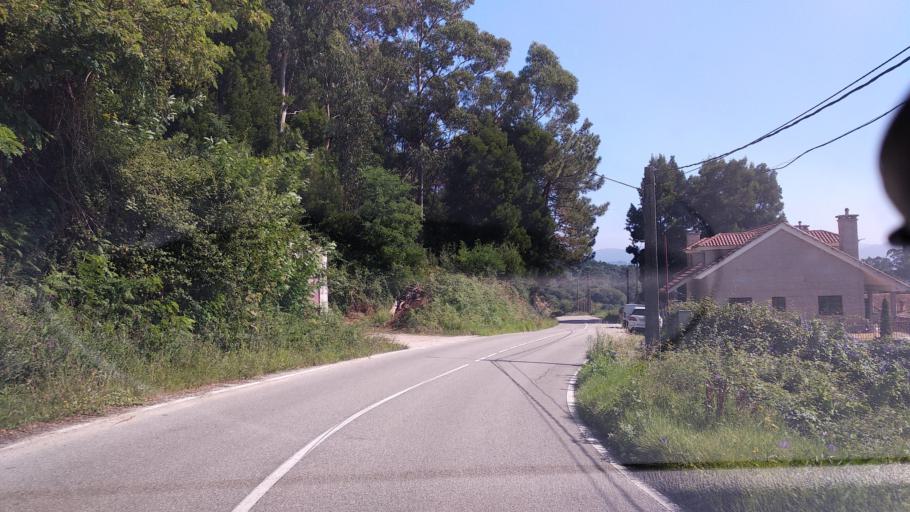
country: ES
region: Galicia
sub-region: Provincia de Pontevedra
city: Moana
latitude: 42.2789
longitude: -8.7665
